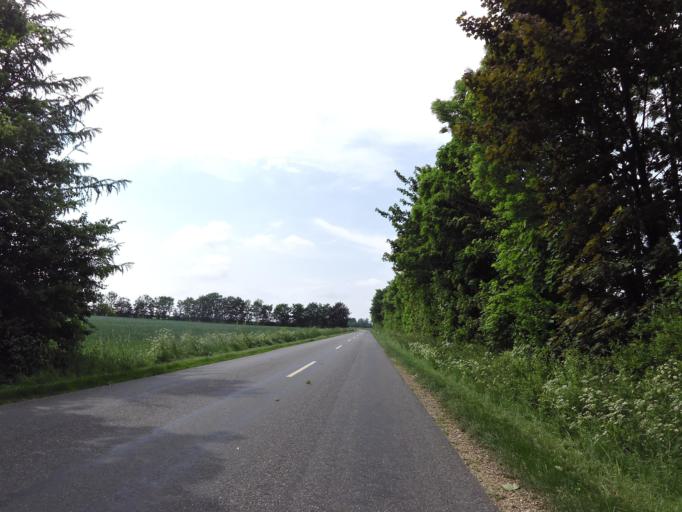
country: DK
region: South Denmark
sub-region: Haderslev Kommune
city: Gram
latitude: 55.2765
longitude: 9.1148
